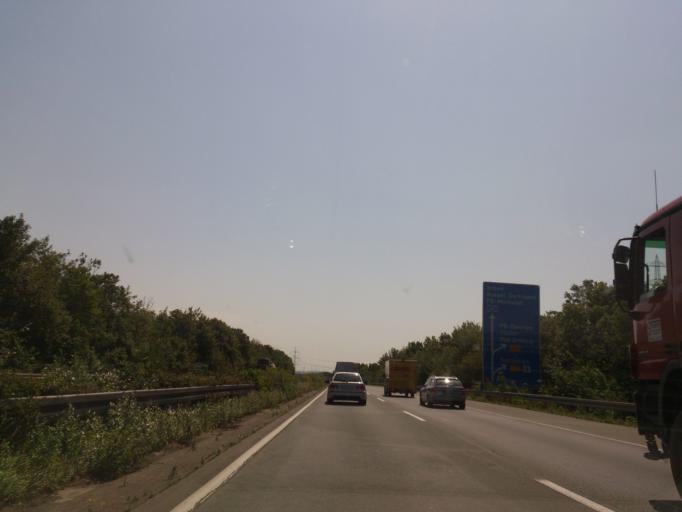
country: DE
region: North Rhine-Westphalia
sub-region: Regierungsbezirk Detmold
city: Paderborn
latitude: 51.7140
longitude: 8.7048
